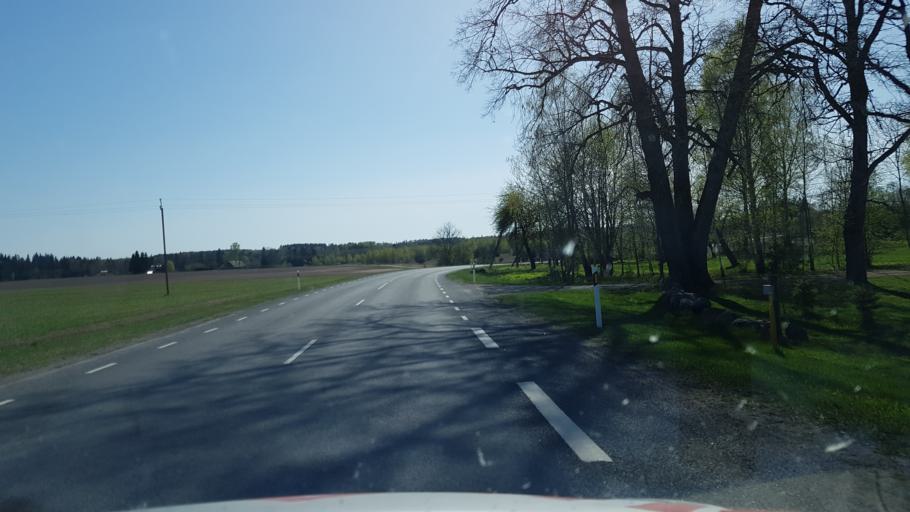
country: EE
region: Viljandimaa
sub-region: Viljandi linn
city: Viljandi
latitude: 58.3143
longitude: 25.5633
